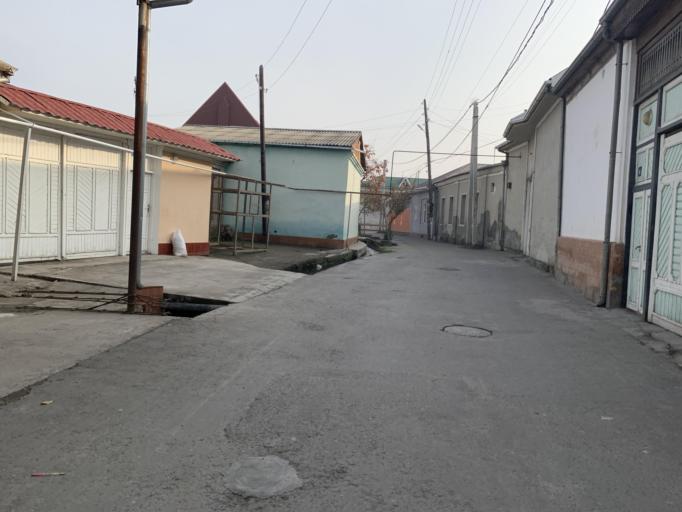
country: UZ
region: Fergana
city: Qo`qon
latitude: 40.5405
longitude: 70.9281
